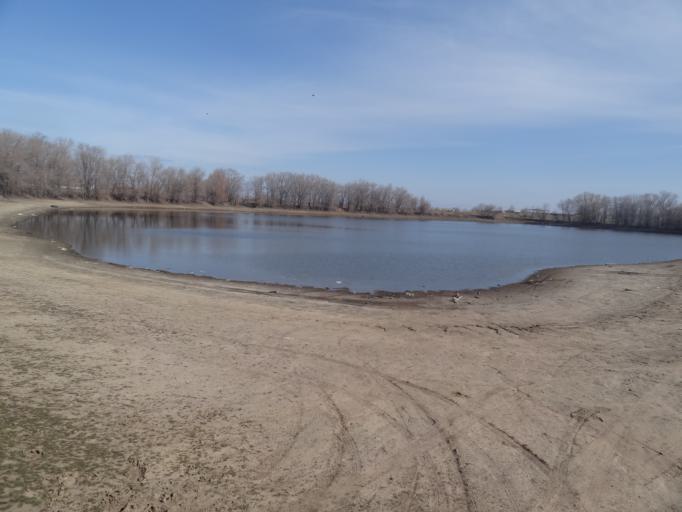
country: RU
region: Saratov
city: Engel's
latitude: 51.4282
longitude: 46.1818
